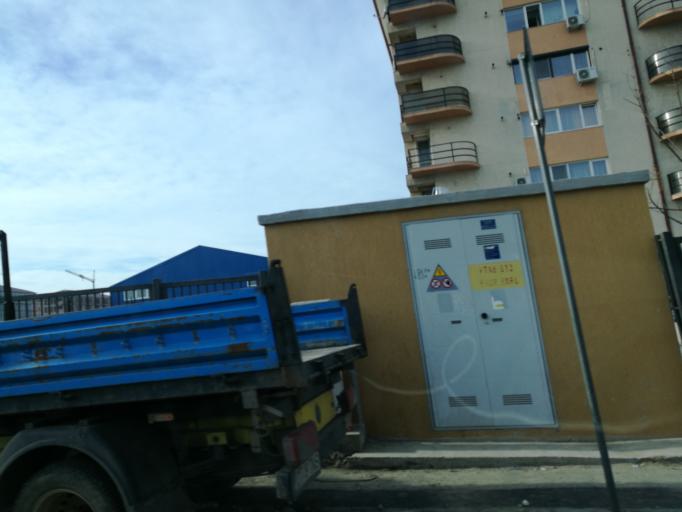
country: RO
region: Constanta
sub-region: Municipiul Constanta
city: Palazu Mare
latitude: 44.1998
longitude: 28.6067
